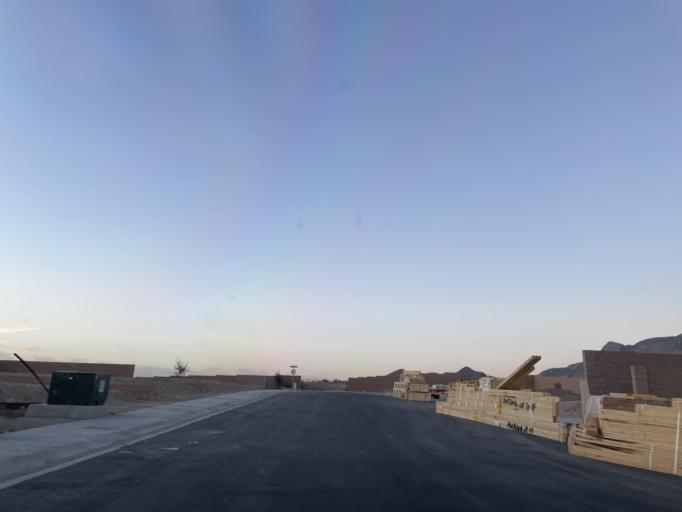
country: US
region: Nevada
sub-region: Clark County
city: Summerlin South
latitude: 36.2598
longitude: -115.3328
